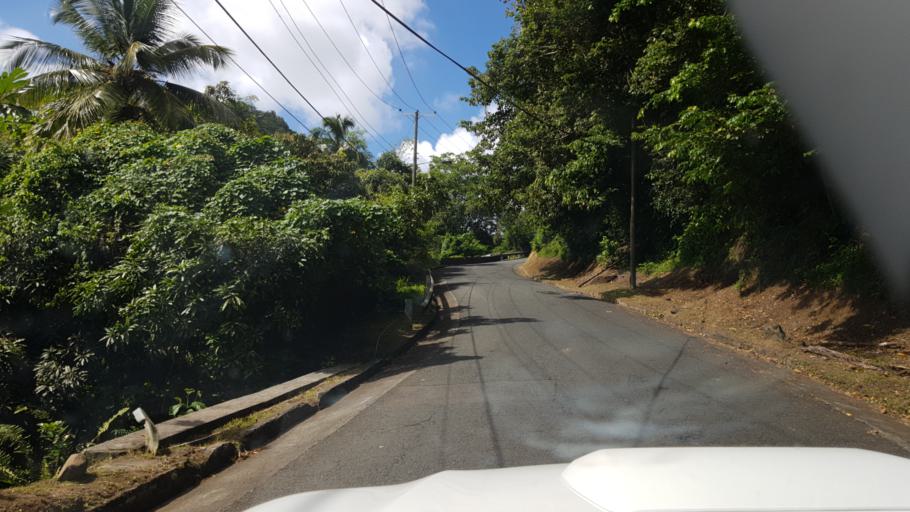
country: LC
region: Castries Quarter
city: Castries
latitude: 13.9897
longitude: -60.9731
